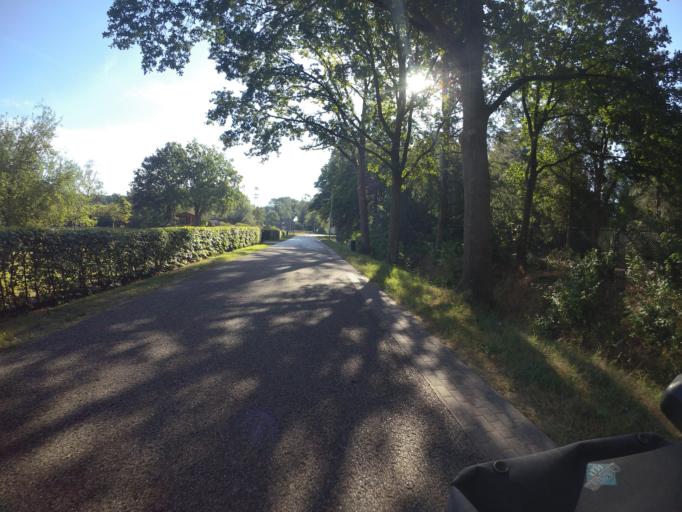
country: NL
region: Overijssel
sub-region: Gemeente Zwolle
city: Zwolle
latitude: 52.5337
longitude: 6.1324
